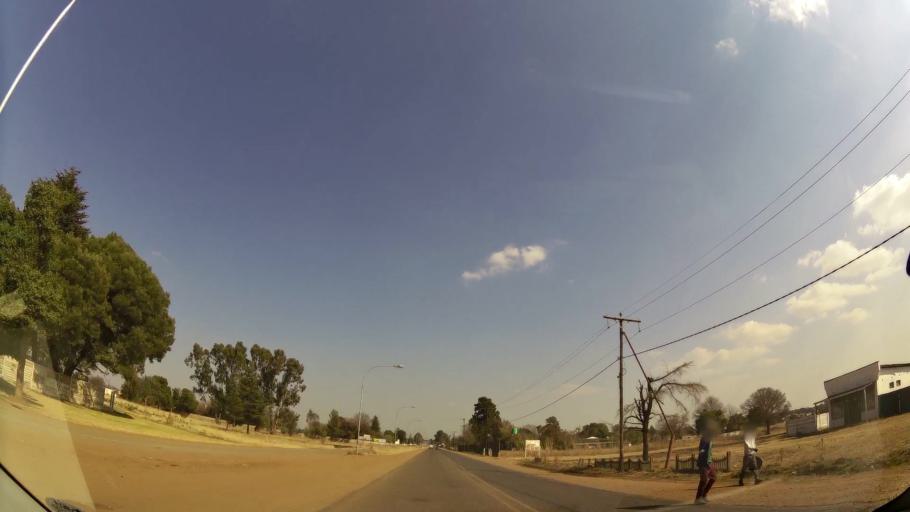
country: ZA
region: Gauteng
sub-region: Ekurhuleni Metropolitan Municipality
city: Benoni
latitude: -26.1179
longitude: 28.4051
